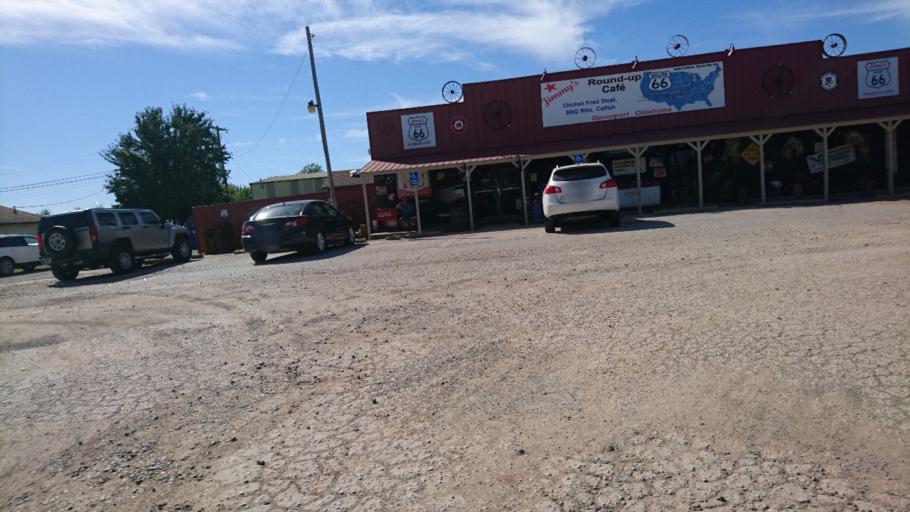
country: US
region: Oklahoma
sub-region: Lincoln County
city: Stroud
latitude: 35.7143
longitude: -96.7653
